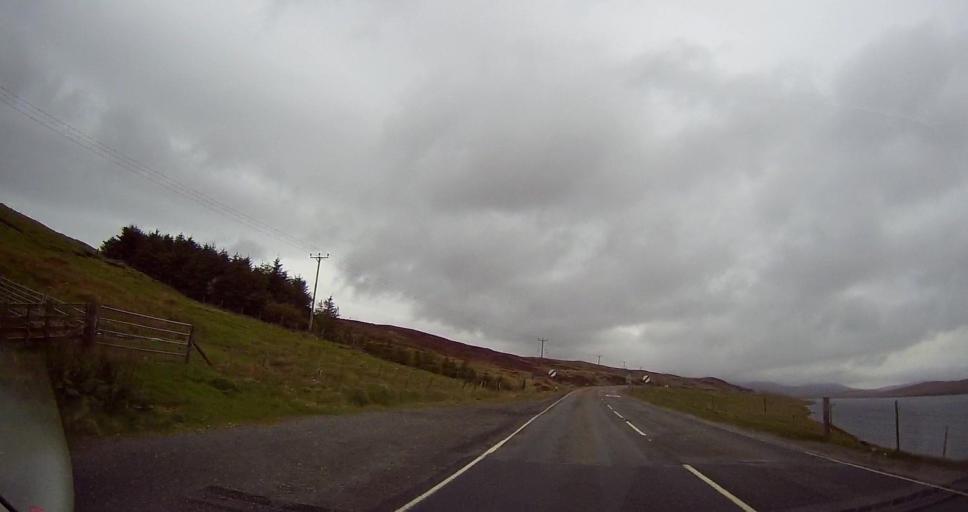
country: GB
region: Scotland
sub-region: Shetland Islands
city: Lerwick
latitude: 60.2413
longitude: -1.2286
